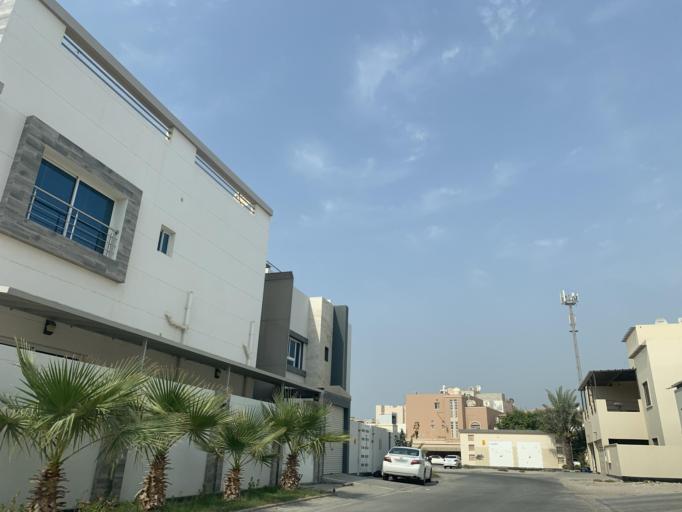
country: BH
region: Manama
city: Jidd Hafs
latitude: 26.2126
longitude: 50.4870
